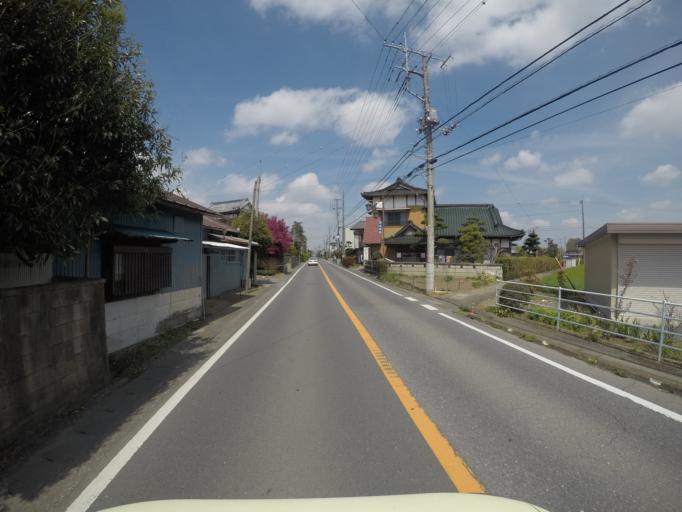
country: JP
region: Ibaraki
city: Makabe
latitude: 36.2529
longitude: 140.0343
